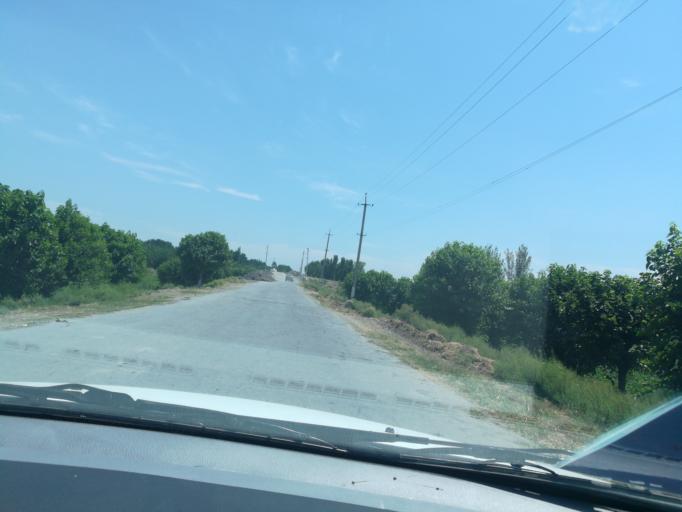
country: UZ
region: Namangan
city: Haqqulobod
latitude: 40.8999
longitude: 72.0009
